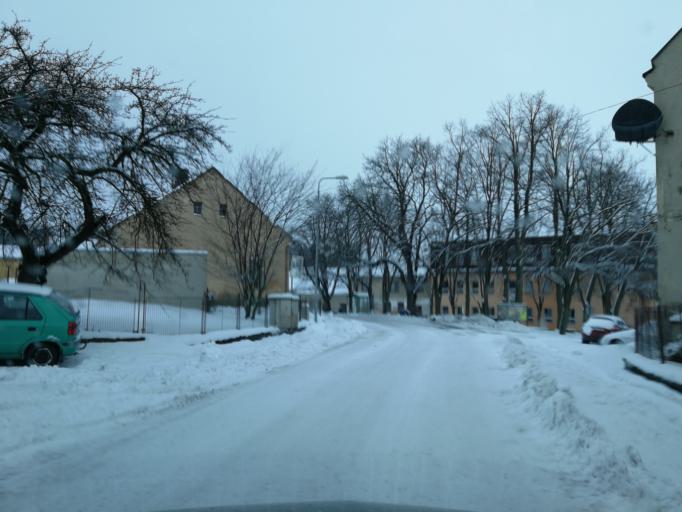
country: CZ
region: Vysocina
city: Heralec
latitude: 49.5302
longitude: 15.4581
